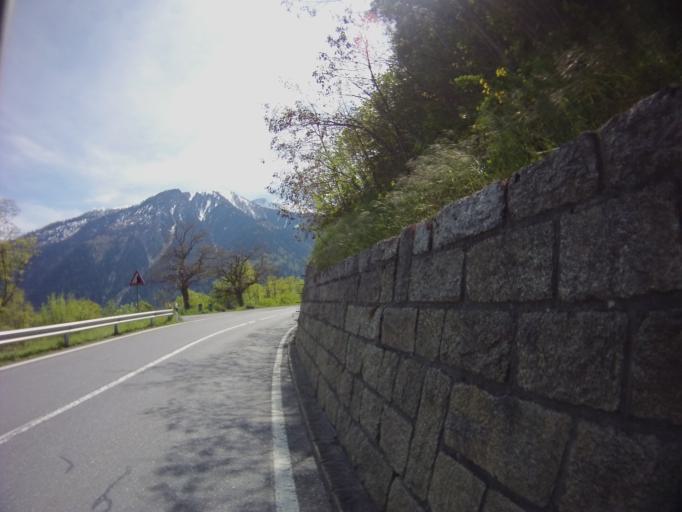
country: CH
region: Valais
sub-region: Martigny District
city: Martigny-Combe
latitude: 46.0892
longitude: 7.0454
